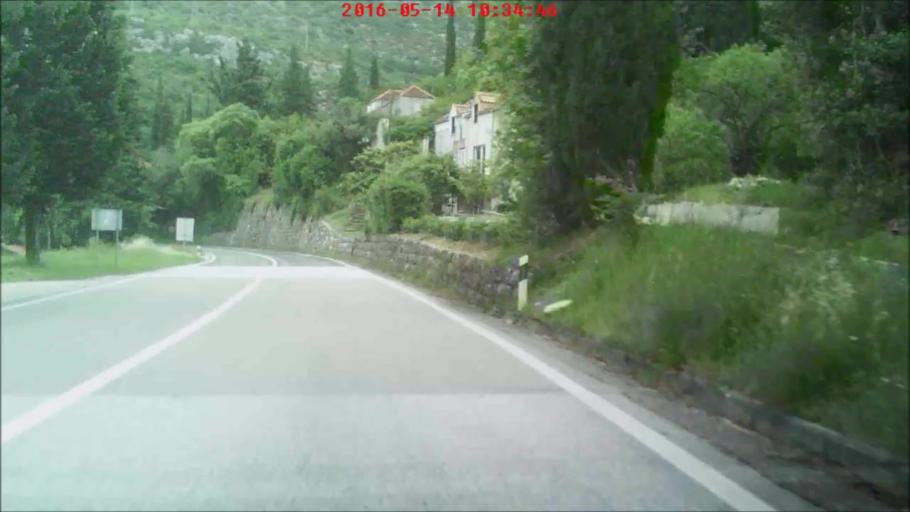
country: HR
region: Dubrovacko-Neretvanska
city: Podgora
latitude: 42.7841
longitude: 17.8932
